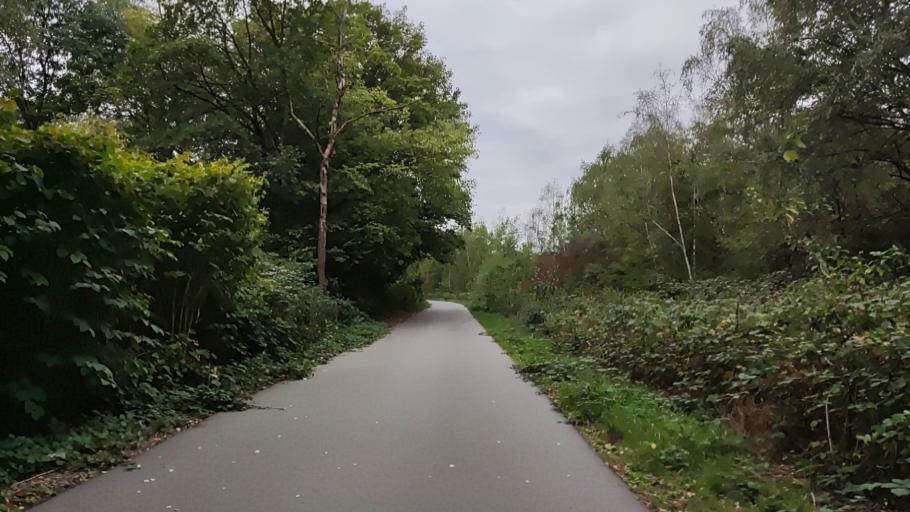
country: DE
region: North Rhine-Westphalia
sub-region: Regierungsbezirk Arnsberg
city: Herne
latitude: 51.5566
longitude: 7.2346
